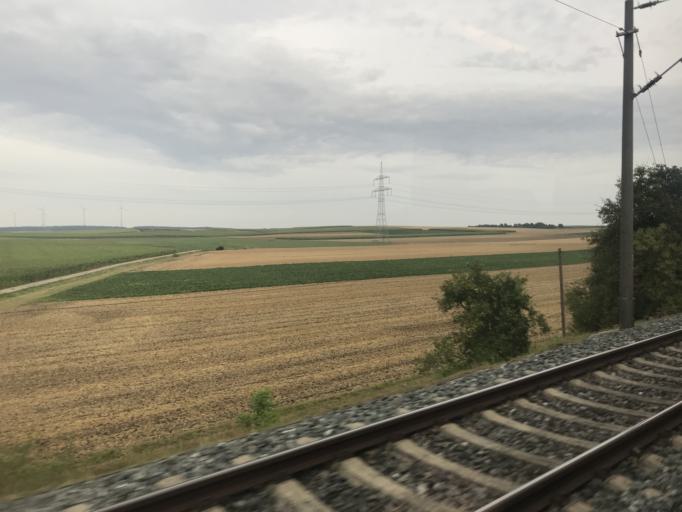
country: DE
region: Bavaria
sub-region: Regierungsbezirk Unterfranken
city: Oberpleichfeld
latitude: 49.8824
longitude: 10.0915
